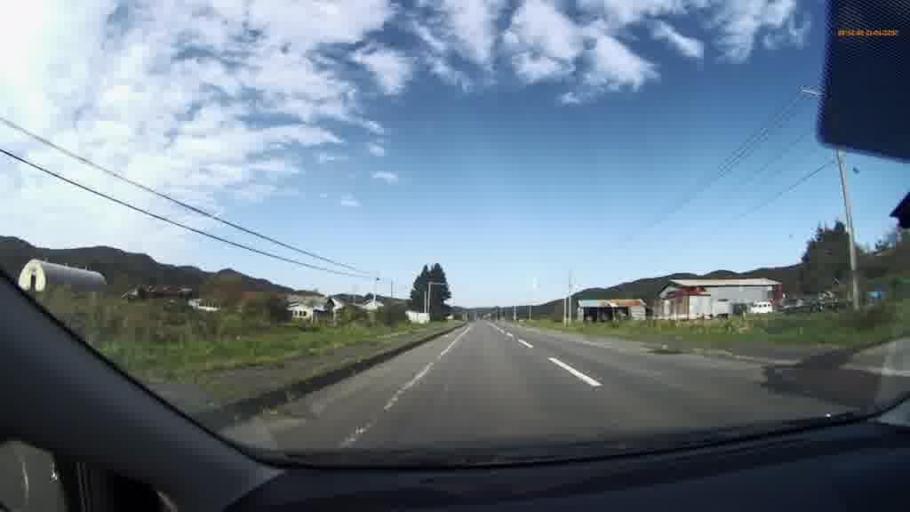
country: JP
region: Hokkaido
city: Kushiro
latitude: 42.9915
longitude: 144.0560
